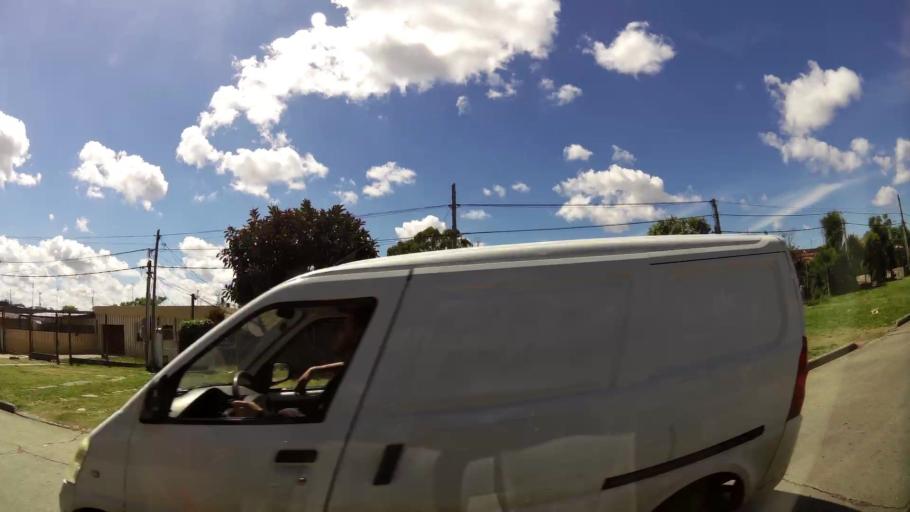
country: UY
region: Canelones
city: Paso de Carrasco
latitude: -34.8346
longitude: -56.1298
